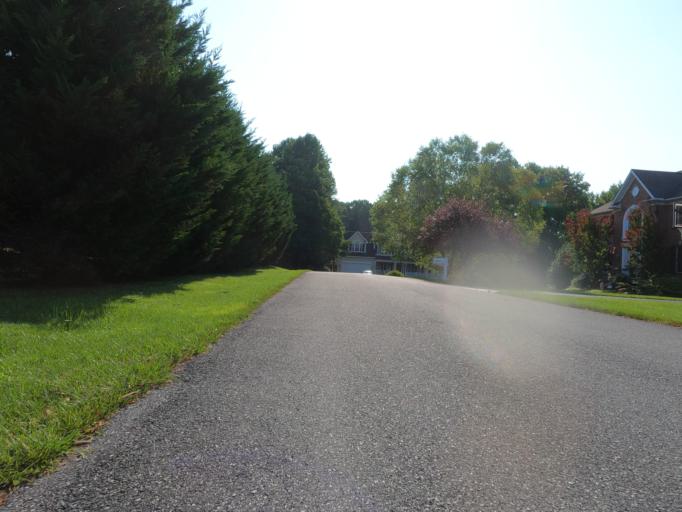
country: US
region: Maryland
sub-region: Anne Arundel County
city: Gambrills
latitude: 39.0604
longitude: -76.6688
